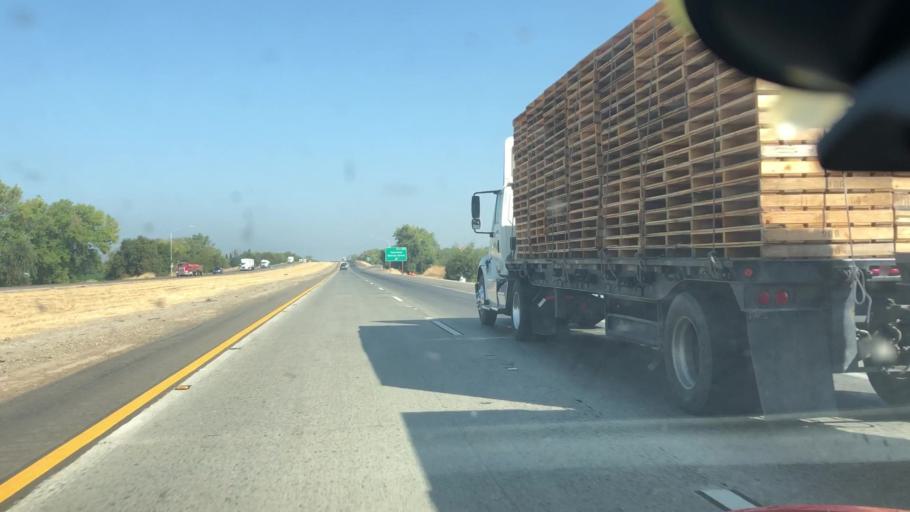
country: US
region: California
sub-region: San Joaquin County
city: Thornton
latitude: 38.2207
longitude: -121.4268
